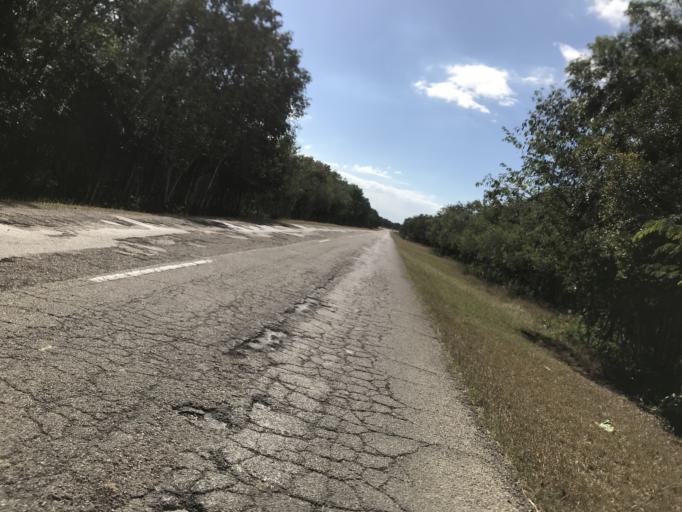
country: CU
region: Cienfuegos
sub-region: Municipio de Aguada de Pasajeros
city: Aguada de Pasajeros
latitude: 22.0712
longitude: -81.0364
